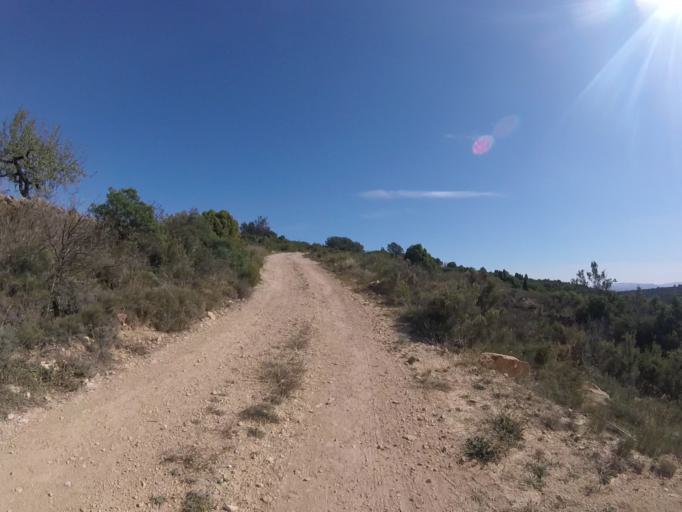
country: ES
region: Valencia
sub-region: Provincia de Castello
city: Sierra-Engarceran
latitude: 40.2725
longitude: 0.0172
